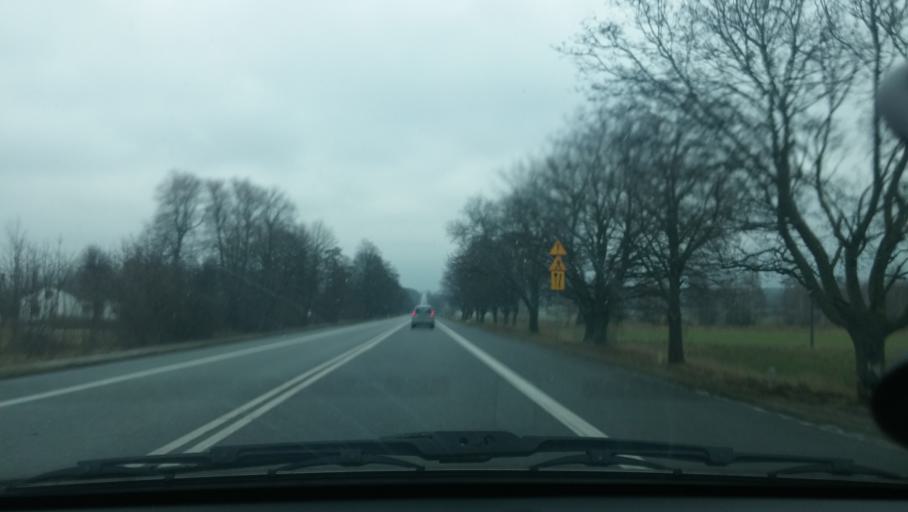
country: PL
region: Masovian Voivodeship
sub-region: Powiat wegrowski
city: Grebkow
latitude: 52.2028
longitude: 21.9645
